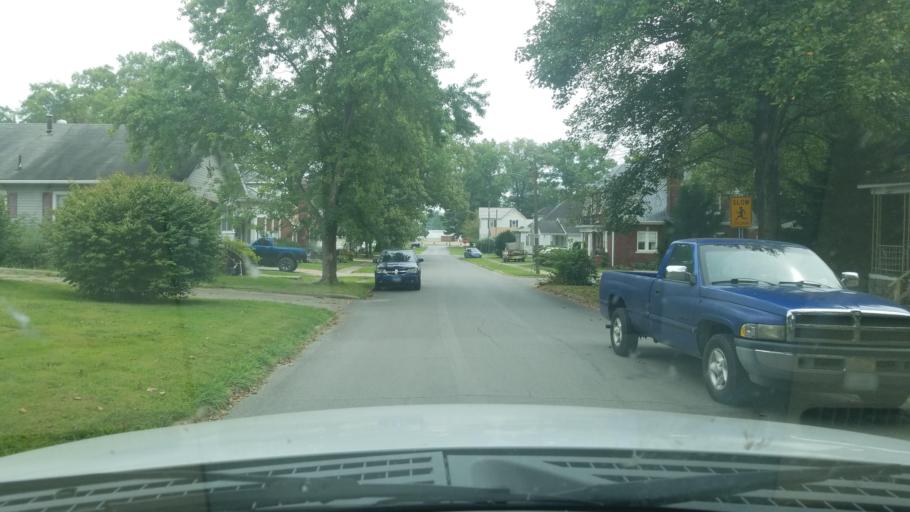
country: US
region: Illinois
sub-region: Saline County
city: Eldorado
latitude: 37.8172
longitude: -88.4395
